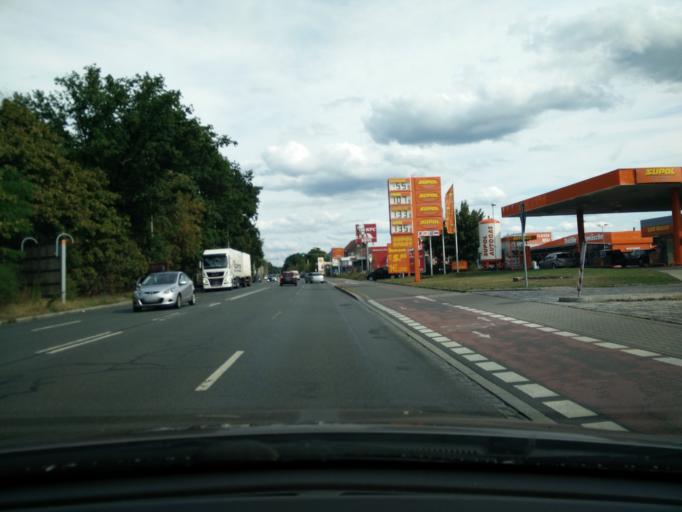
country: DE
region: Bavaria
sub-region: Regierungsbezirk Mittelfranken
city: Nuernberg
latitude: 49.4350
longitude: 11.1244
